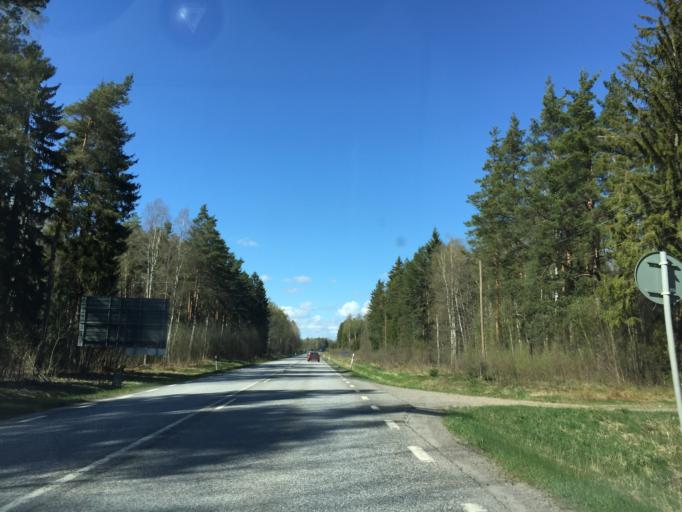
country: SE
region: OErebro
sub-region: Hallsbergs Kommun
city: Skollersta
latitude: 59.1371
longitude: 15.2812
